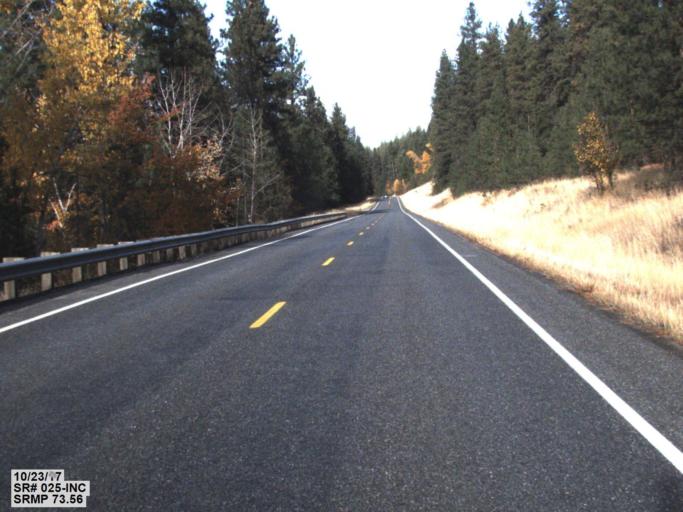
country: US
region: Washington
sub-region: Stevens County
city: Kettle Falls
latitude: 48.5209
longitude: -118.1402
